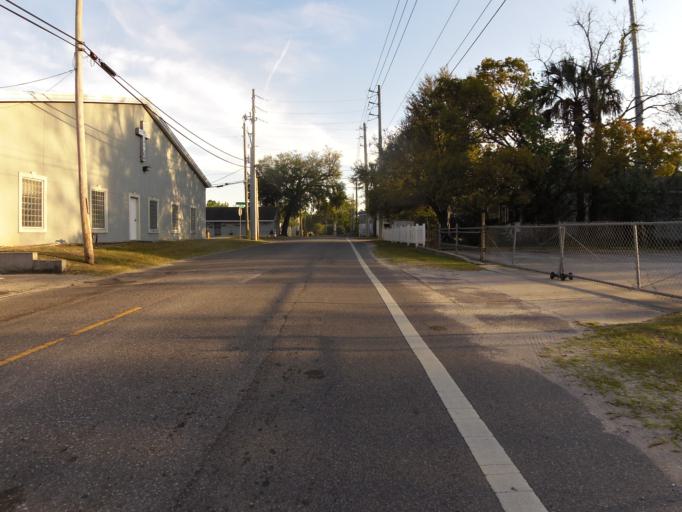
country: US
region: Florida
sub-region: Duval County
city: Jacksonville
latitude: 30.2993
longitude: -81.6428
